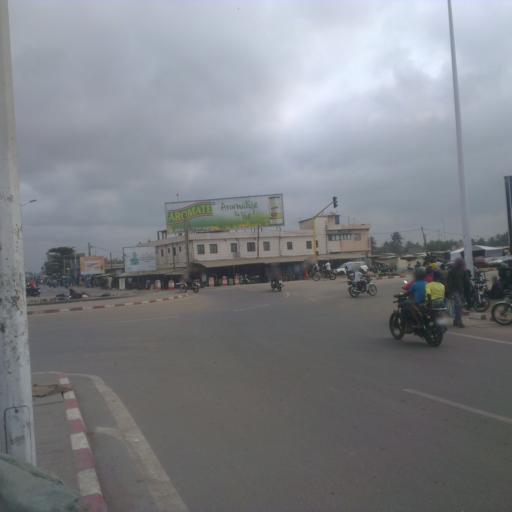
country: TG
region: Maritime
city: Lome
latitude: 6.1585
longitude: 1.2851
